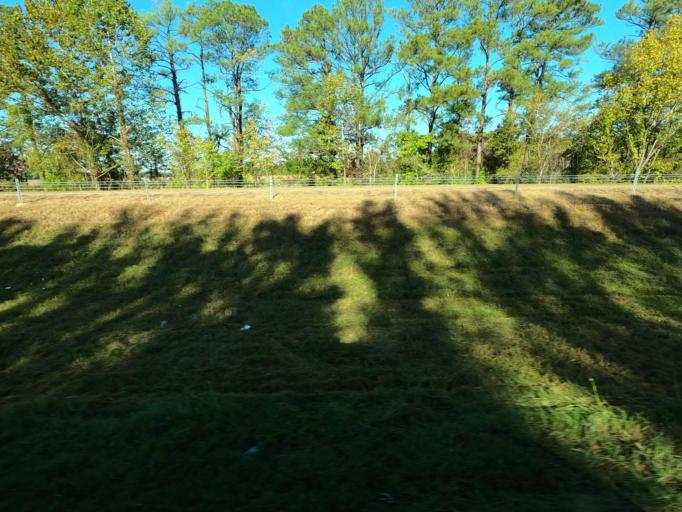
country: US
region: Tennessee
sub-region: Tipton County
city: Brighton
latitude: 35.5014
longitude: -89.7183
